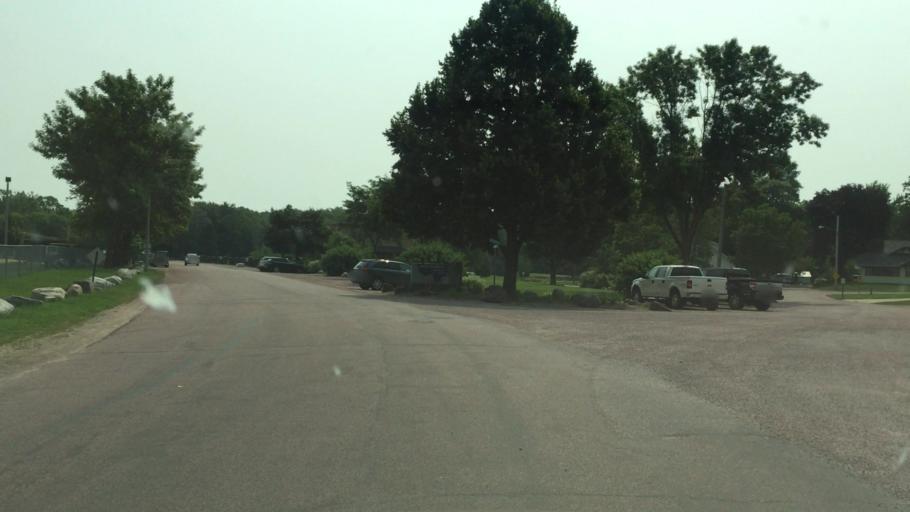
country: US
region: Iowa
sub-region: Dickinson County
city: Milford
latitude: 43.3494
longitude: -95.1583
